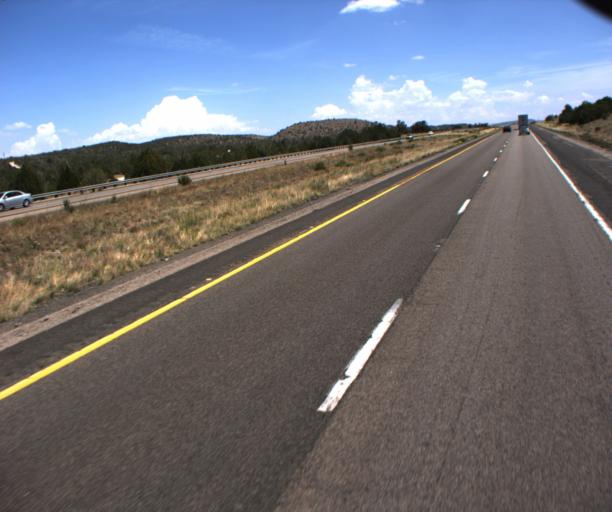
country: US
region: Arizona
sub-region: Mohave County
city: Peach Springs
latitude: 35.2959
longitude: -113.0273
